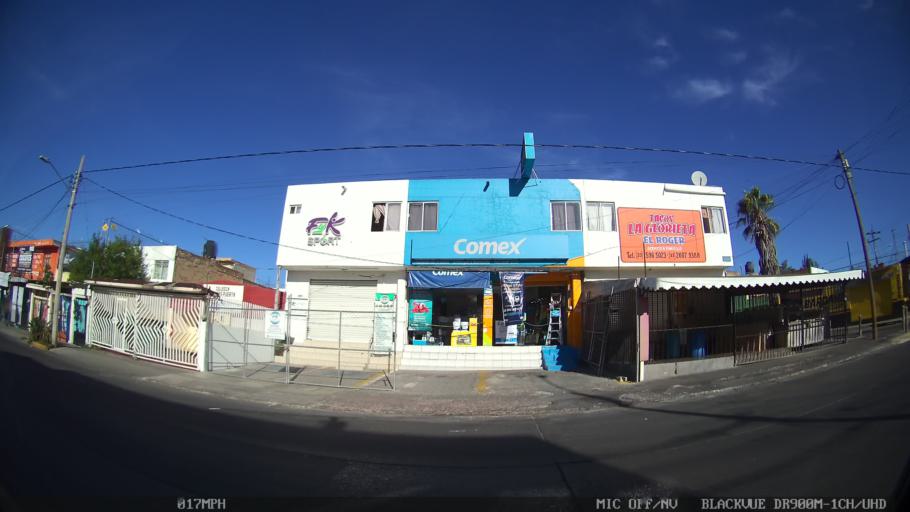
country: MX
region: Jalisco
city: Tlaquepaque
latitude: 20.6973
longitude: -103.2944
